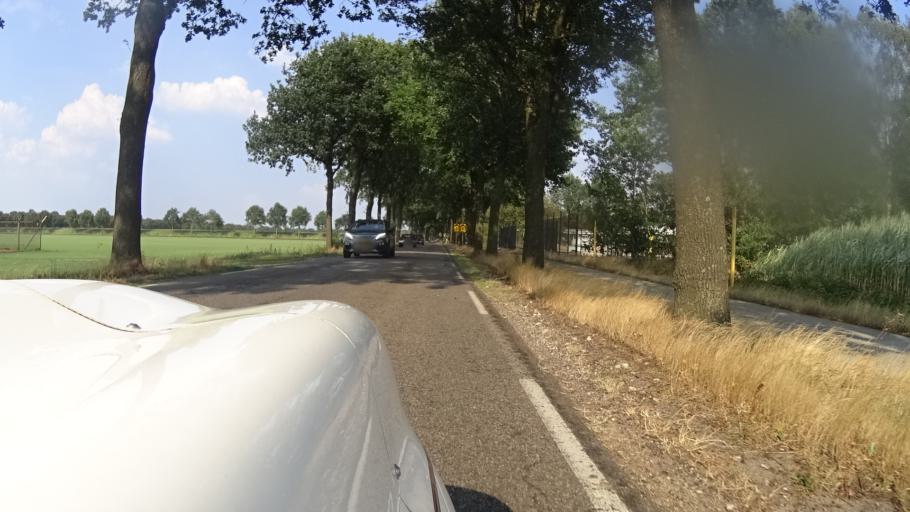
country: NL
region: North Brabant
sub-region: Gemeente Mill en Sint Hubert
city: Wilbertoord
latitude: 51.6176
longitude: 5.7854
